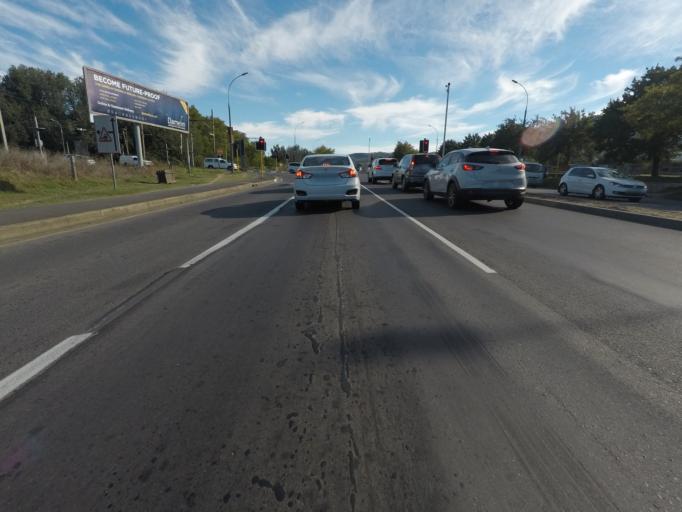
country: ZA
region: Western Cape
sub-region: Cape Winelands District Municipality
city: Stellenbosch
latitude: -33.9348
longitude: 18.8523
